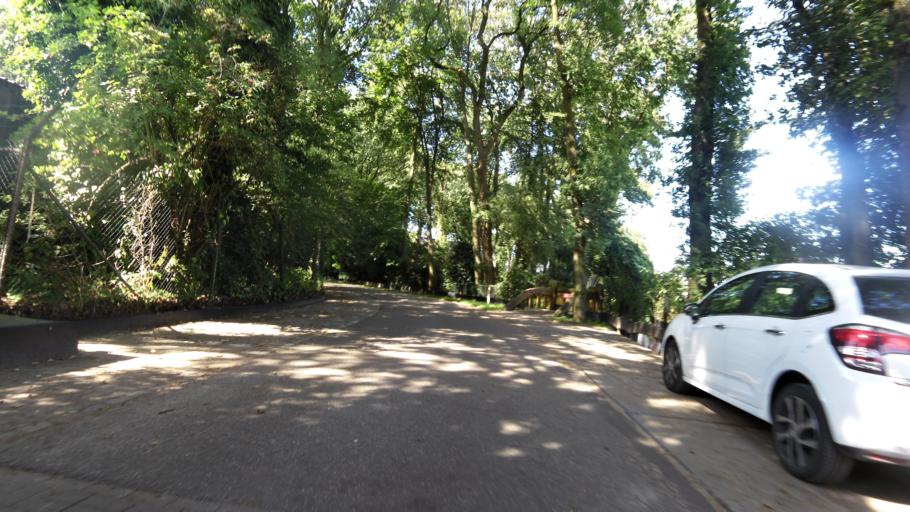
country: NL
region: Gelderland
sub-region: Gemeente Ede
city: Harskamp
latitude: 52.1362
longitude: 5.7599
